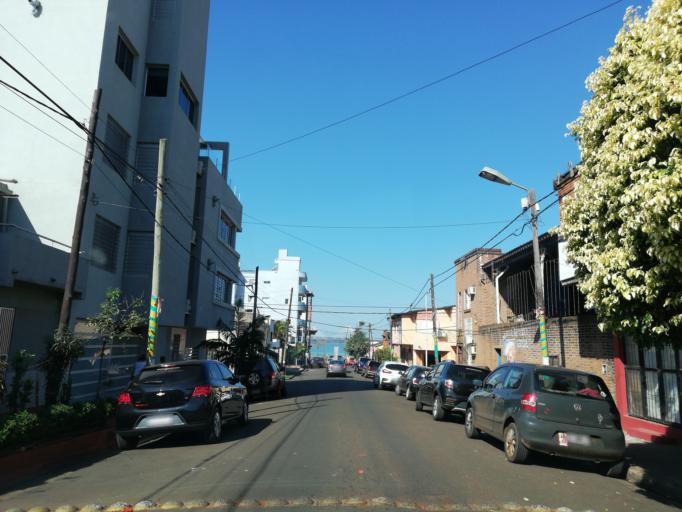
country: AR
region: Misiones
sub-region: Departamento de Capital
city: Posadas
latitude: -27.3669
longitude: -55.8863
